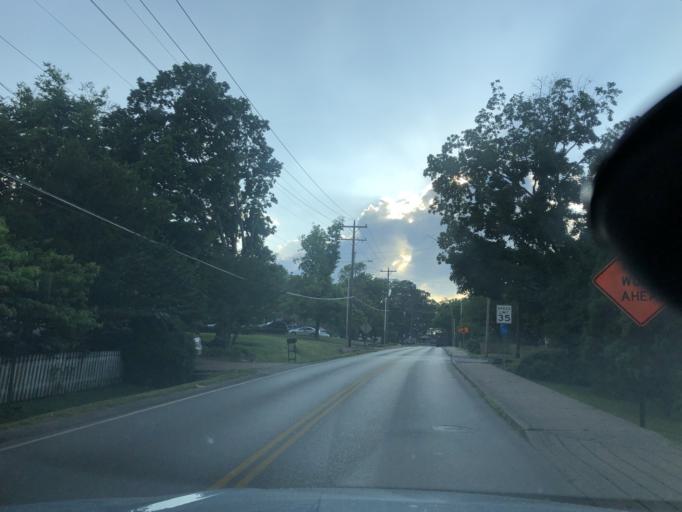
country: US
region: Tennessee
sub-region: Davidson County
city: Oak Hill
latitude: 36.1018
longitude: -86.8069
